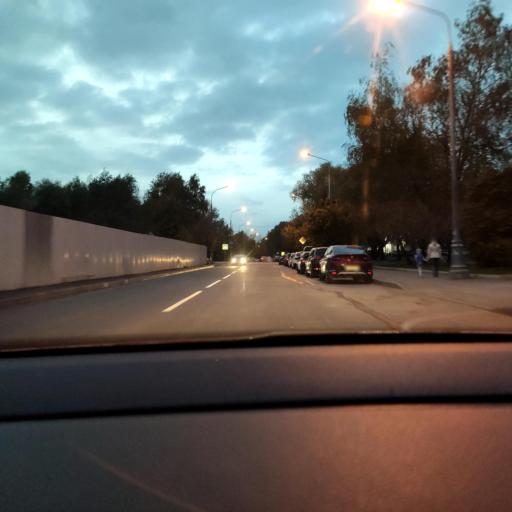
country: RU
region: Moscow
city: Zagor'ye
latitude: 55.5737
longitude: 37.6714
